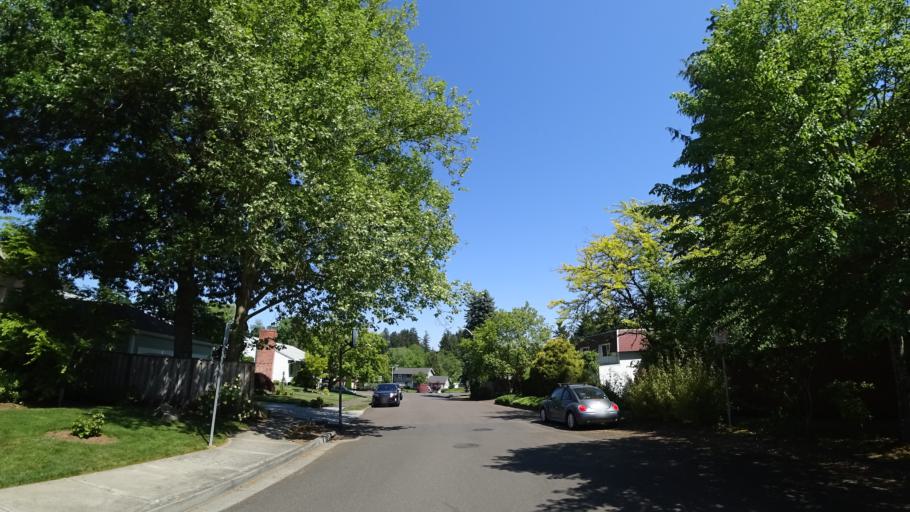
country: US
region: Oregon
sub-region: Washington County
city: Cedar Hills
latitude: 45.4963
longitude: -122.7974
